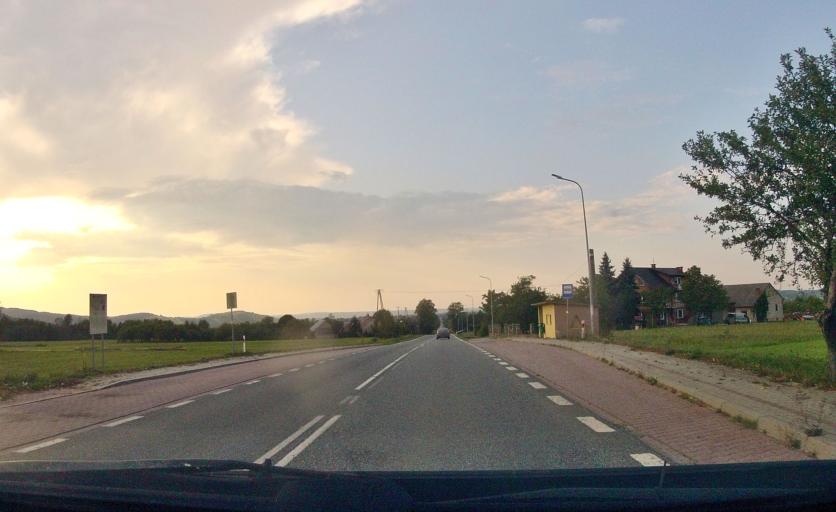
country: PL
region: Subcarpathian Voivodeship
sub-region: Powiat jasielski
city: Nowy Zmigrod
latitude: 49.5869
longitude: 21.5456
